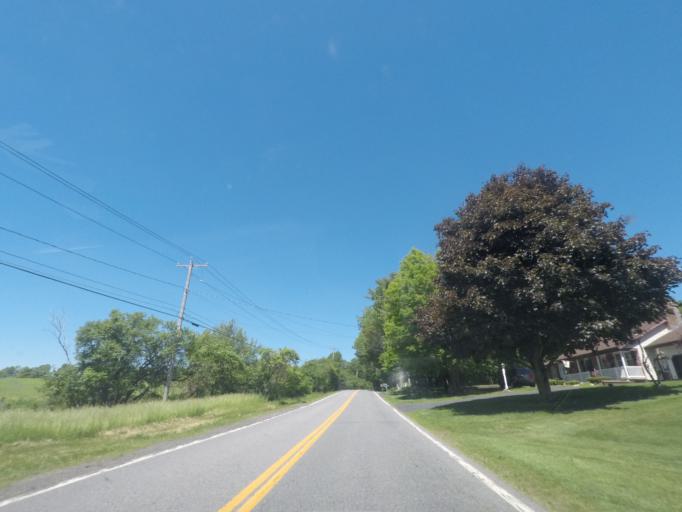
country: US
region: New York
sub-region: Saratoga County
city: Country Knolls
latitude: 42.8732
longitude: -73.8549
